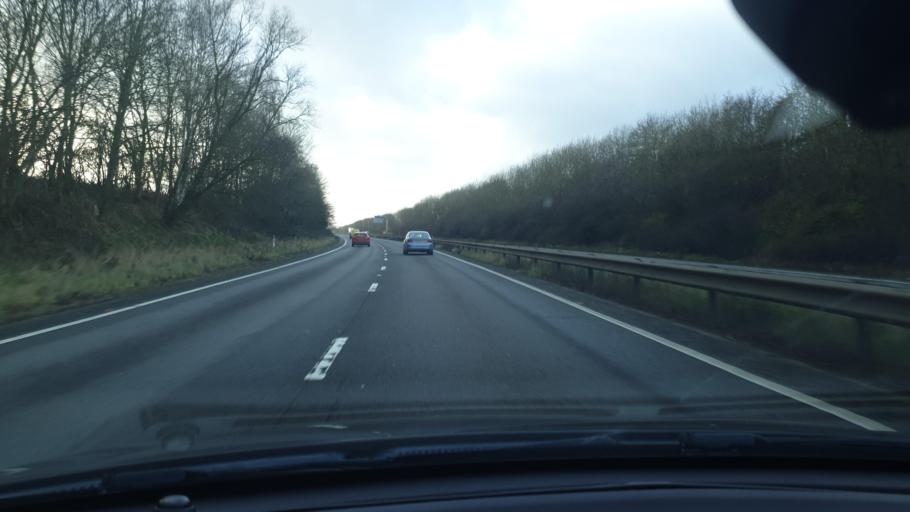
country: GB
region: England
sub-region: Northamptonshire
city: Burton Latimer
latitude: 52.3789
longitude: -0.6677
